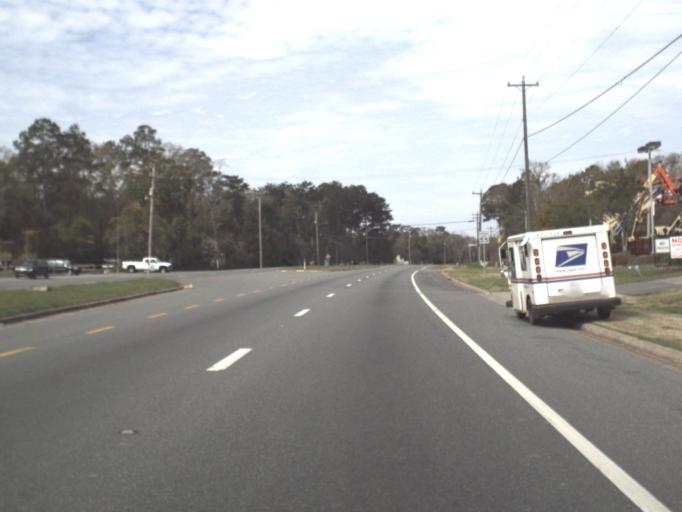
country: US
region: Florida
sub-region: Gadsden County
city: Midway
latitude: 30.4575
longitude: -84.3812
